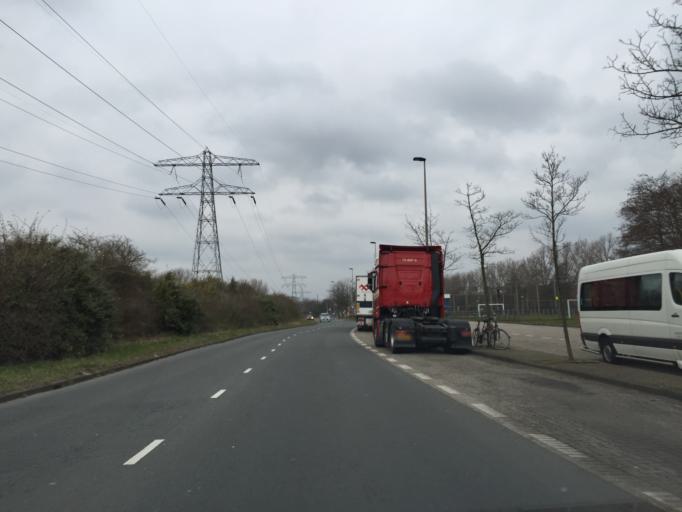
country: NL
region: South Holland
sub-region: Gemeente Delft
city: Delft
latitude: 51.9835
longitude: 4.3679
